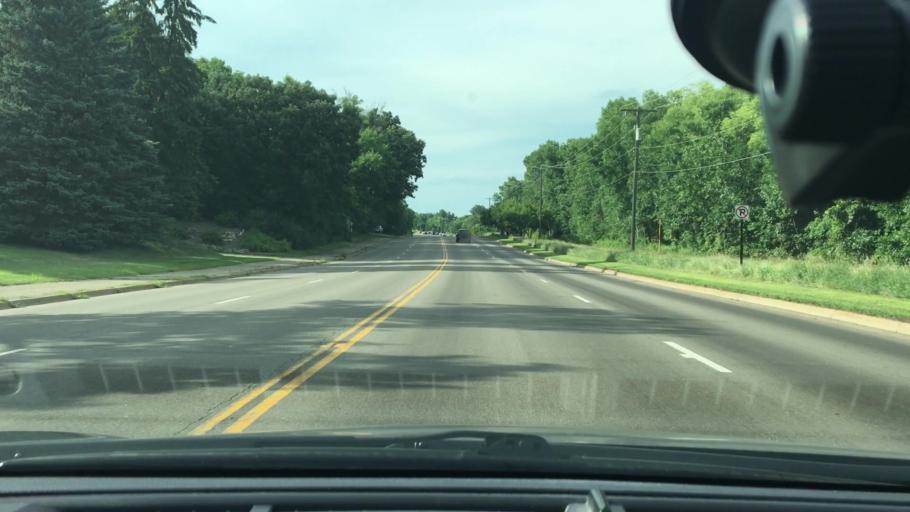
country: US
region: Minnesota
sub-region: Hennepin County
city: Plymouth
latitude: 45.0232
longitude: -93.4426
